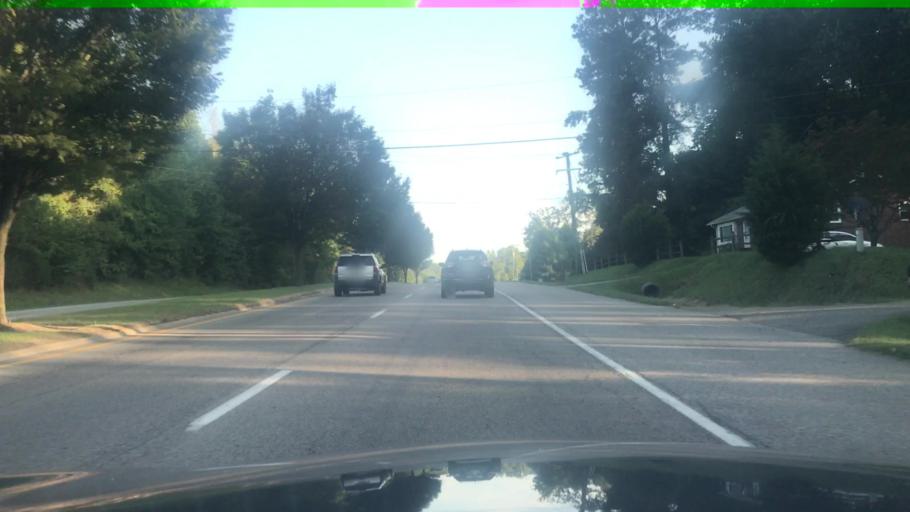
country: US
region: Virginia
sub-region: Chesterfield County
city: Brandermill
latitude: 37.4536
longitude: -77.5875
